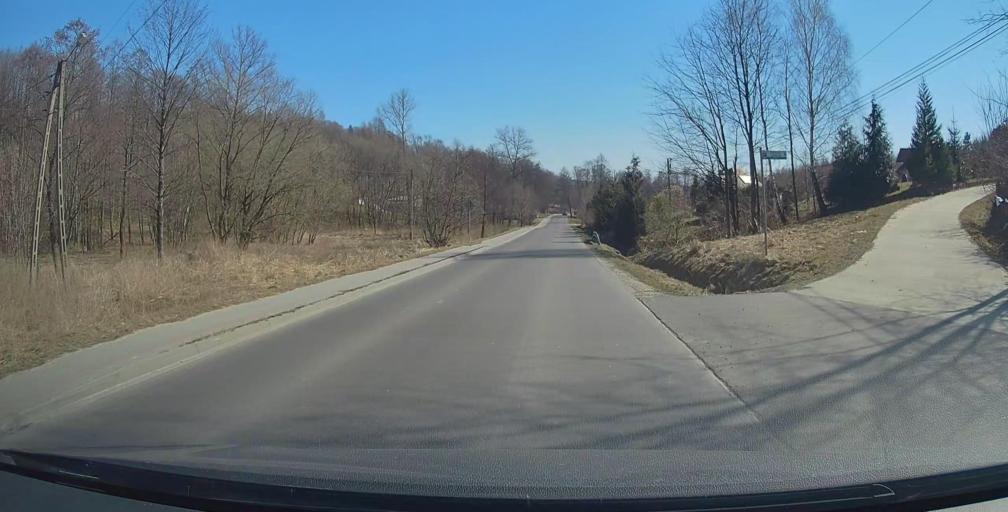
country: PL
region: Subcarpathian Voivodeship
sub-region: Powiat przeworski
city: Jawornik Polski
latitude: 49.8851
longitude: 22.2355
